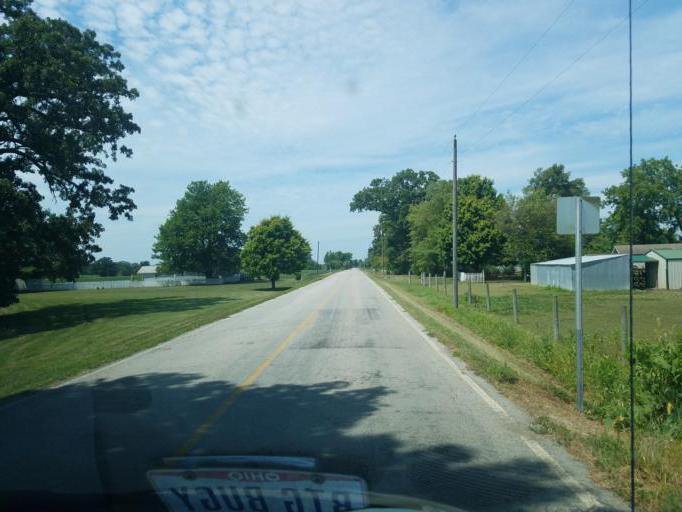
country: US
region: Ohio
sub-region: Madison County
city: West Jefferson
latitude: 40.0072
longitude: -83.2977
